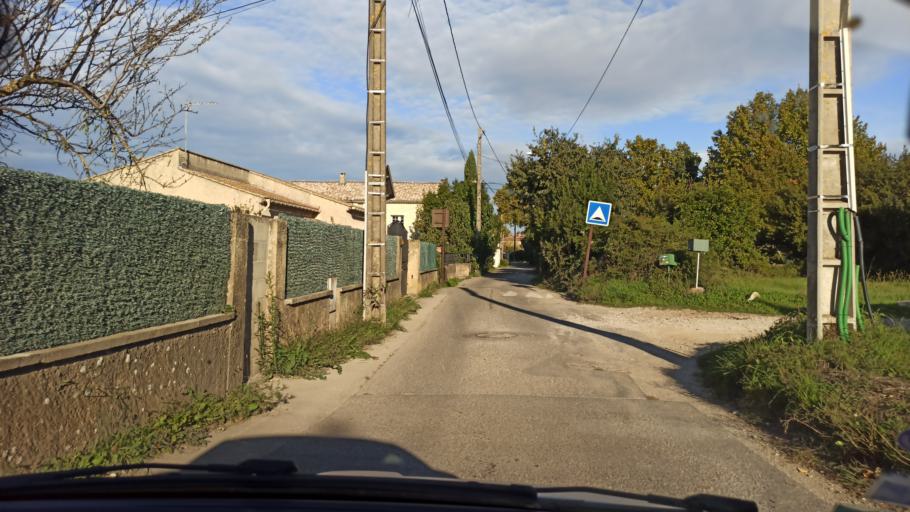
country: FR
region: Provence-Alpes-Cote d'Azur
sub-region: Departement du Vaucluse
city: Montfavet
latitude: 43.9331
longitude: 4.8848
